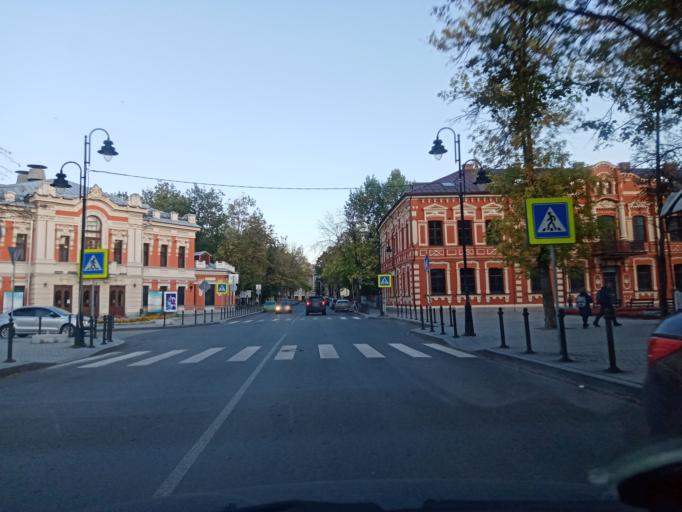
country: RU
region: Pskov
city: Pskov
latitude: 57.8172
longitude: 28.3382
